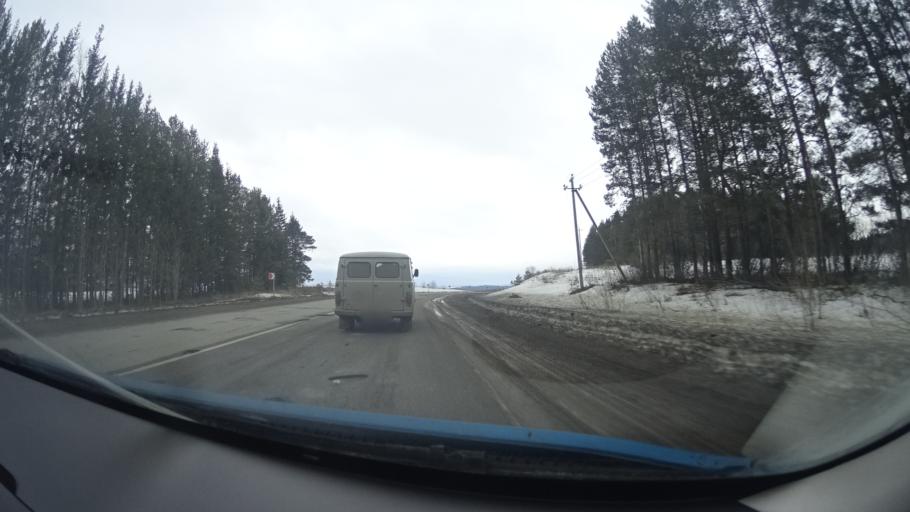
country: RU
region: Perm
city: Osa
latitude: 57.3171
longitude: 55.6224
